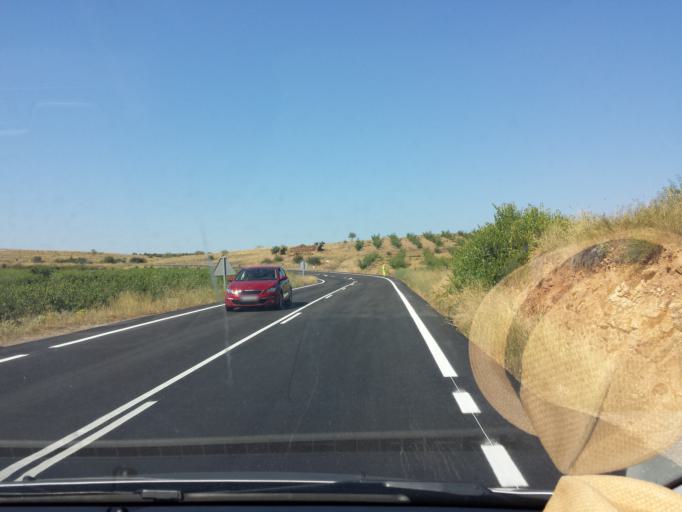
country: ES
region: Aragon
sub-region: Provincia de Zaragoza
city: Munebrega
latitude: 41.2312
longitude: -1.7288
